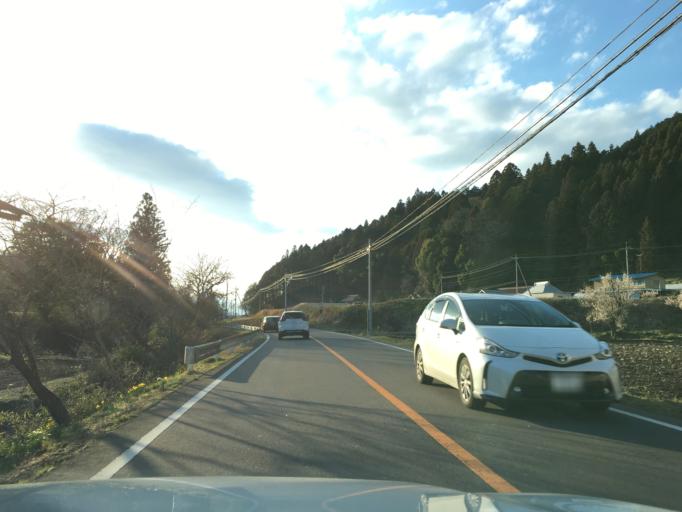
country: JP
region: Tochigi
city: Otawara
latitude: 36.8655
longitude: 140.1643
